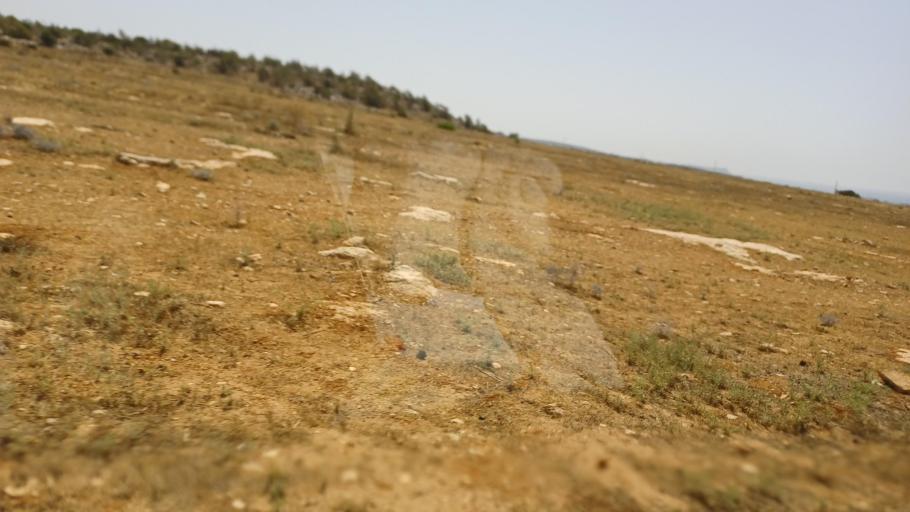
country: CY
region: Ammochostos
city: Paralimni
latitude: 35.0091
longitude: 33.9683
